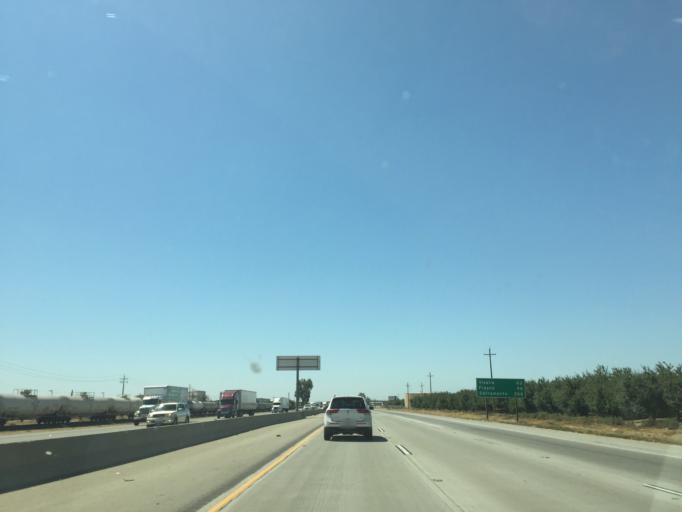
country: US
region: California
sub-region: Kern County
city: Rosedale
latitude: 35.4925
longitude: -119.1548
